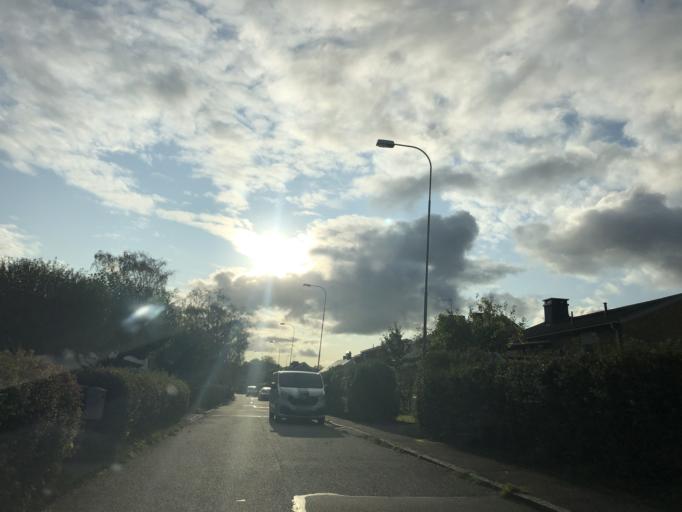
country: SE
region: Vaestra Goetaland
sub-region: Goteborg
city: Majorna
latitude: 57.6631
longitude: 11.8801
